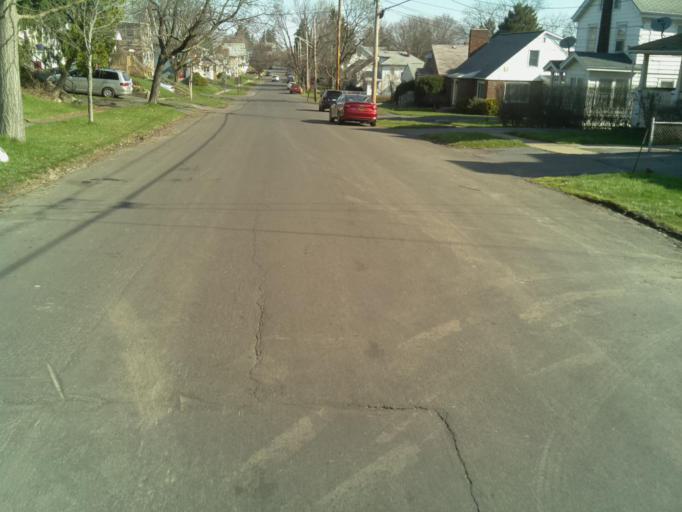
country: US
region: New York
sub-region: Onondaga County
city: Lyncourt
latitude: 43.0659
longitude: -76.1072
